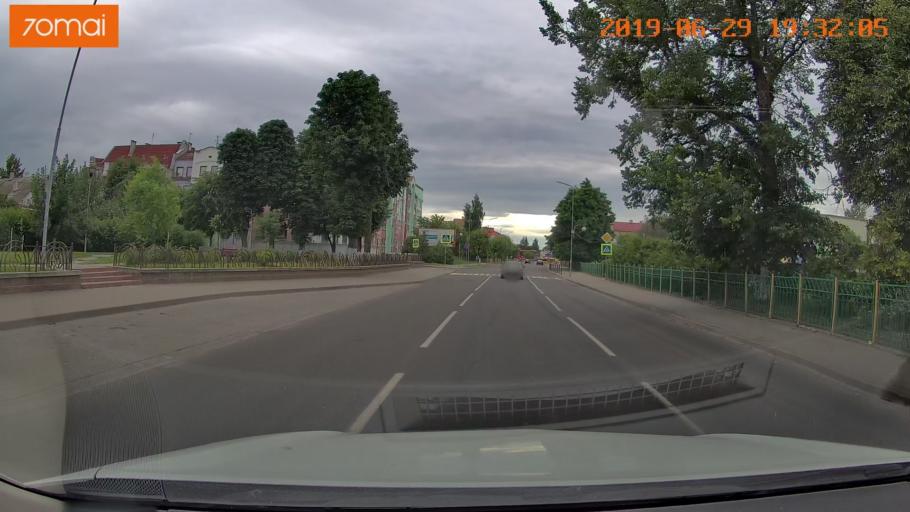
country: BY
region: Brest
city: Pinsk
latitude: 52.1158
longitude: 26.1068
